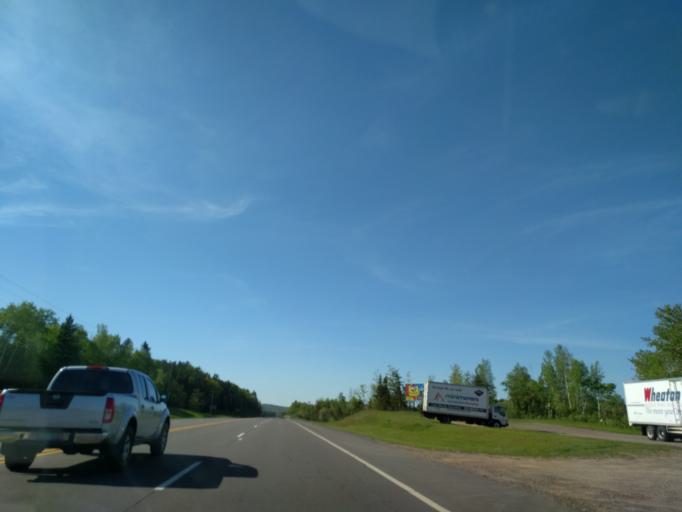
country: US
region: Michigan
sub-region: Marquette County
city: K. I. Sawyer Air Force Base
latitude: 46.4197
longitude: -87.4091
